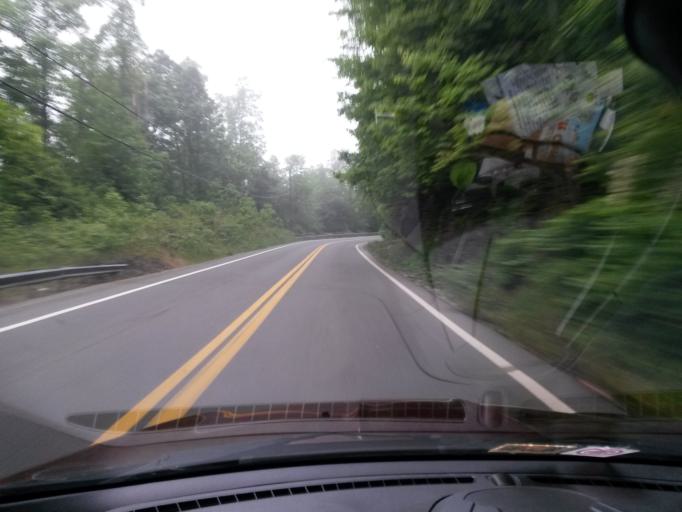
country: US
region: West Virginia
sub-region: Wyoming County
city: Pineville
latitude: 37.5554
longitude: -81.5439
